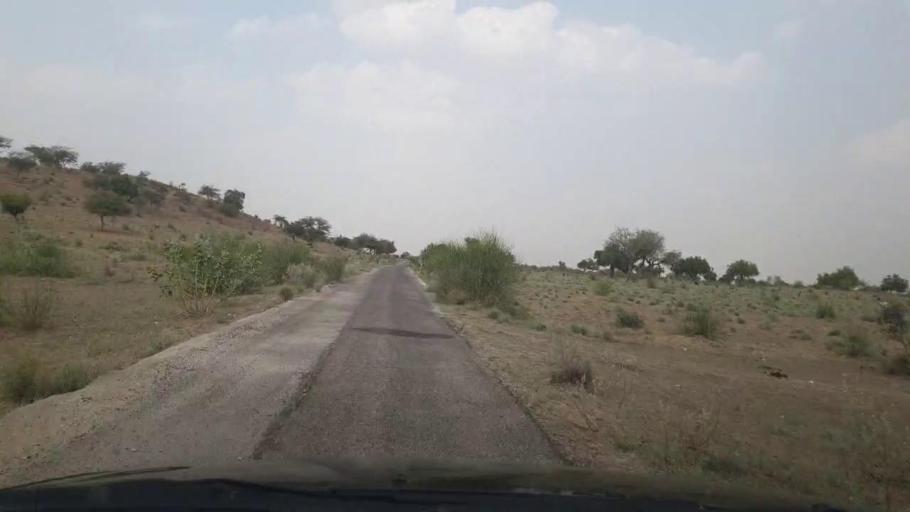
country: PK
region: Sindh
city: Islamkot
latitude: 24.9202
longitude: 70.5632
